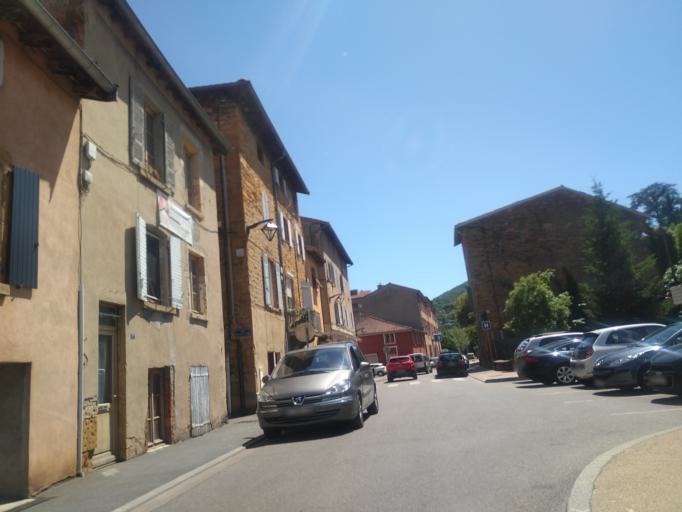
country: FR
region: Rhone-Alpes
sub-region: Departement du Rhone
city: Rochetaillee-sur-Saone
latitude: 45.8449
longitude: 4.8315
